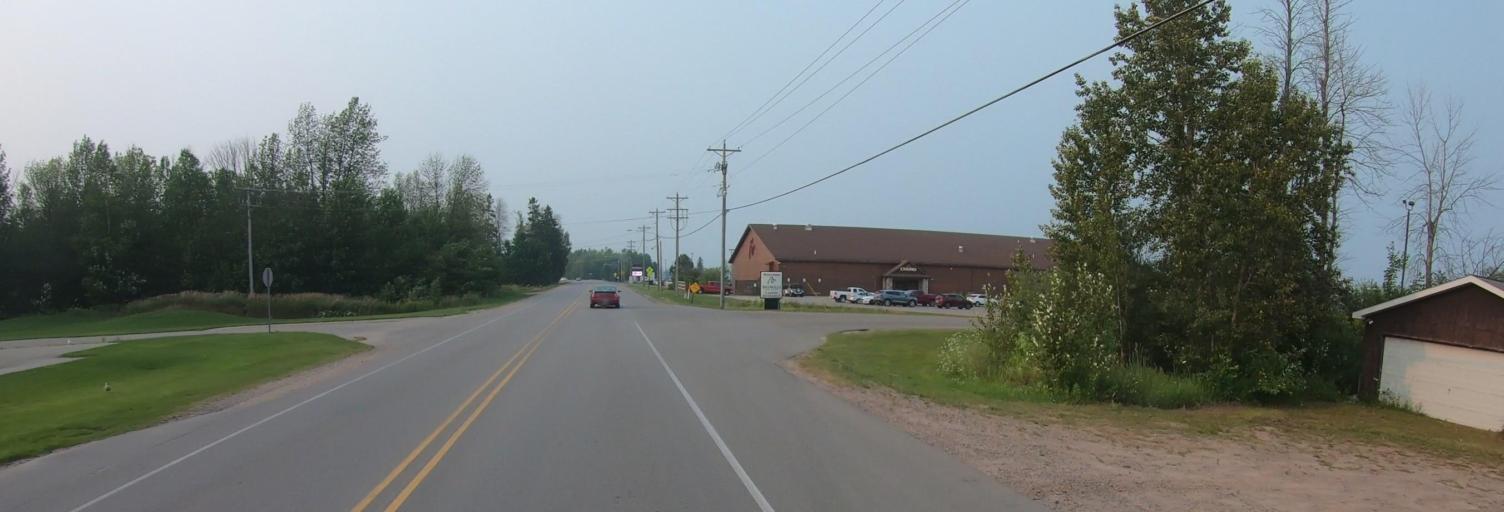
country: US
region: Michigan
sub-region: Chippewa County
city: Sault Ste. Marie
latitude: 46.4209
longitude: -84.6037
